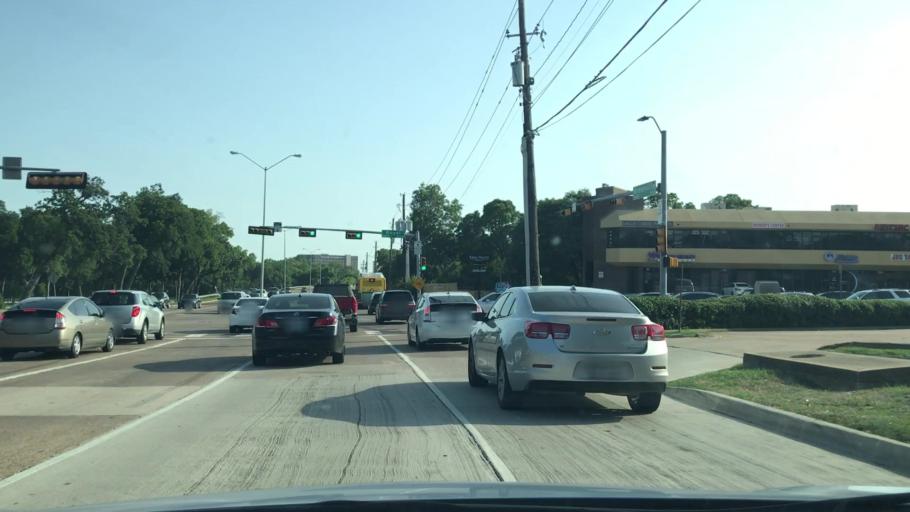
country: US
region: Texas
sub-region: Dallas County
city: Richardson
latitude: 32.8940
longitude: -96.7533
